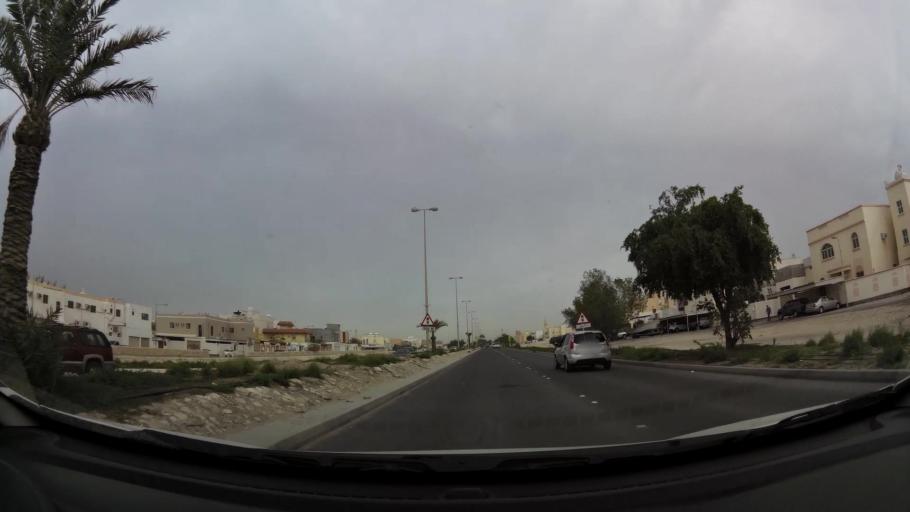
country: BH
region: Central Governorate
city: Dar Kulayb
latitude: 26.0635
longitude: 50.5078
